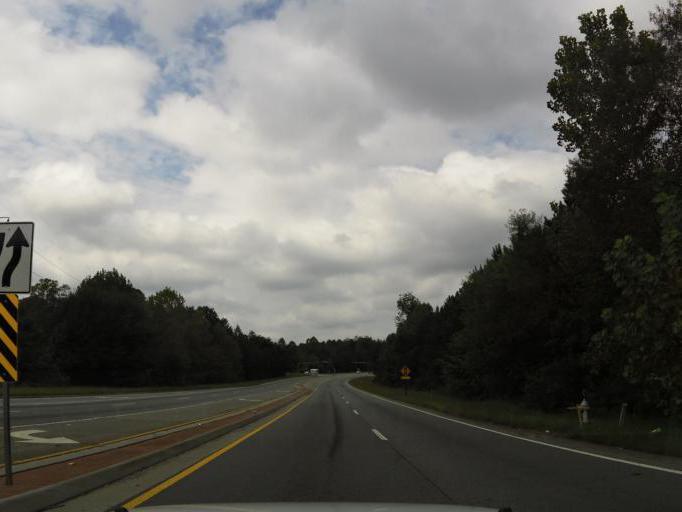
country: US
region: Georgia
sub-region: Cobb County
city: Powder Springs
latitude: 33.8693
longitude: -84.6334
